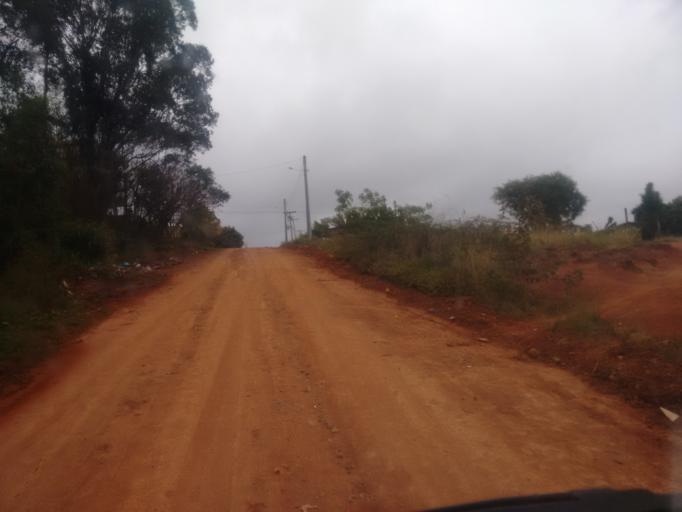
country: BR
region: Rio Grande do Sul
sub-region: Camaqua
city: Camaqua
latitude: -30.8347
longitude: -51.8181
